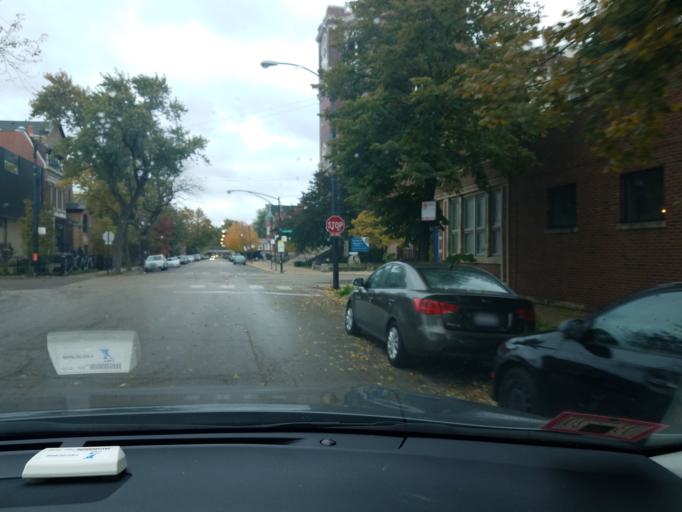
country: US
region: Illinois
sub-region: Cook County
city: Chicago
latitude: 41.9163
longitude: -87.6715
